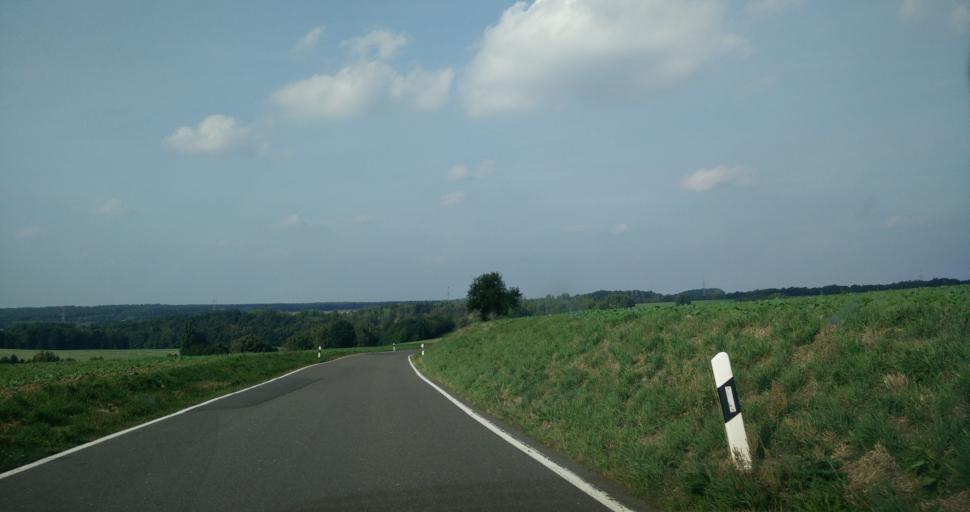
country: DE
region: Saxony
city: Colditz
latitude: 51.0937
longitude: 12.7985
